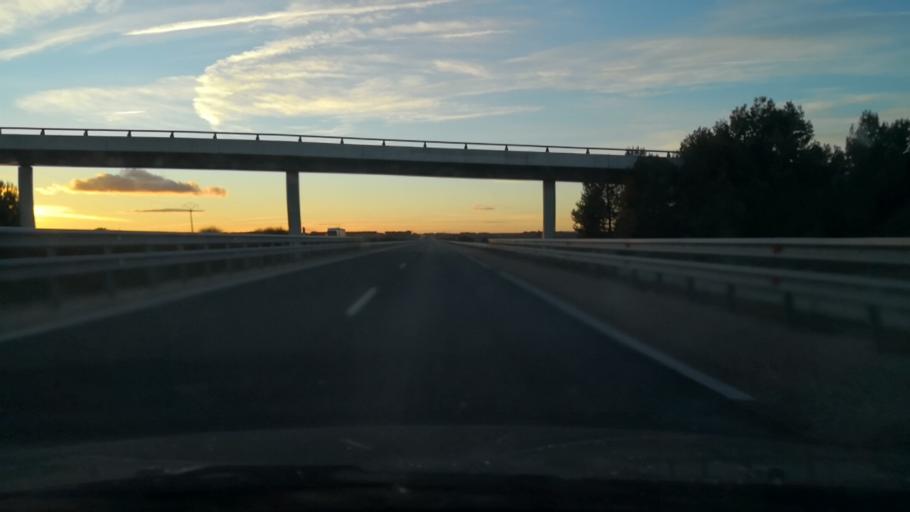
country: ES
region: Castille and Leon
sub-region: Provincia de Valladolid
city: Torrecilla de la Abadesa
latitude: 41.5061
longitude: -5.0654
